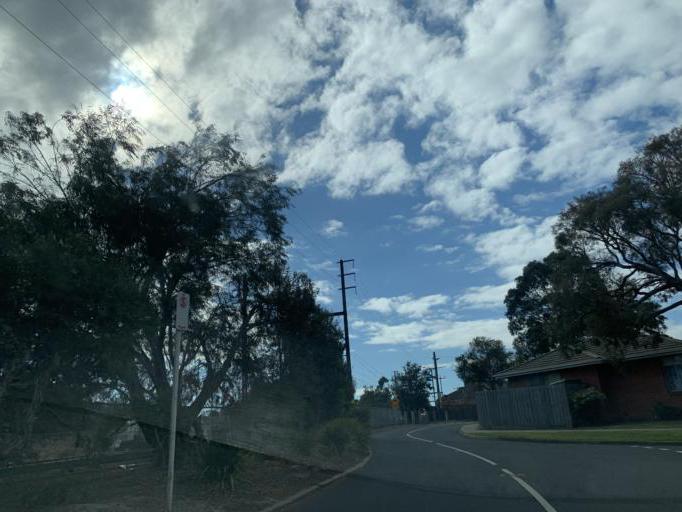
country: AU
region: Victoria
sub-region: Bayside
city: Cheltenham
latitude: -37.9692
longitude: 145.0565
